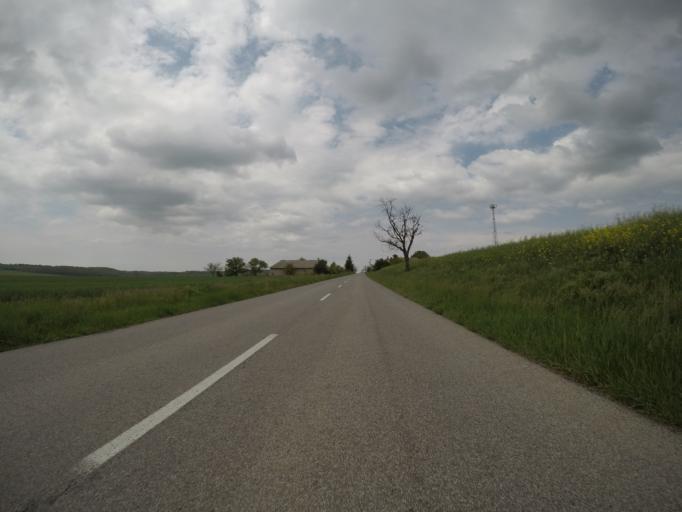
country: SK
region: Banskobystricky
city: Dudince
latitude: 48.0751
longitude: 18.8276
